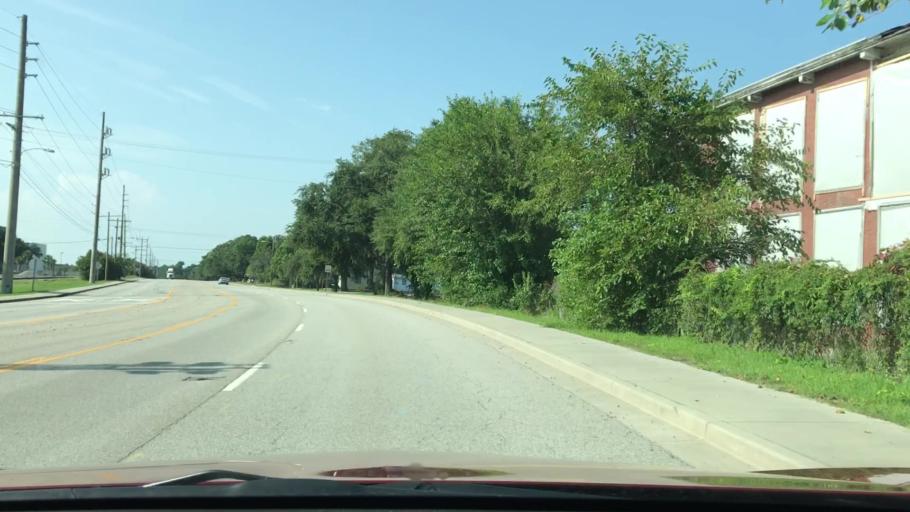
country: US
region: South Carolina
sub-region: Charleston County
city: North Charleston
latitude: 32.8836
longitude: -79.9741
